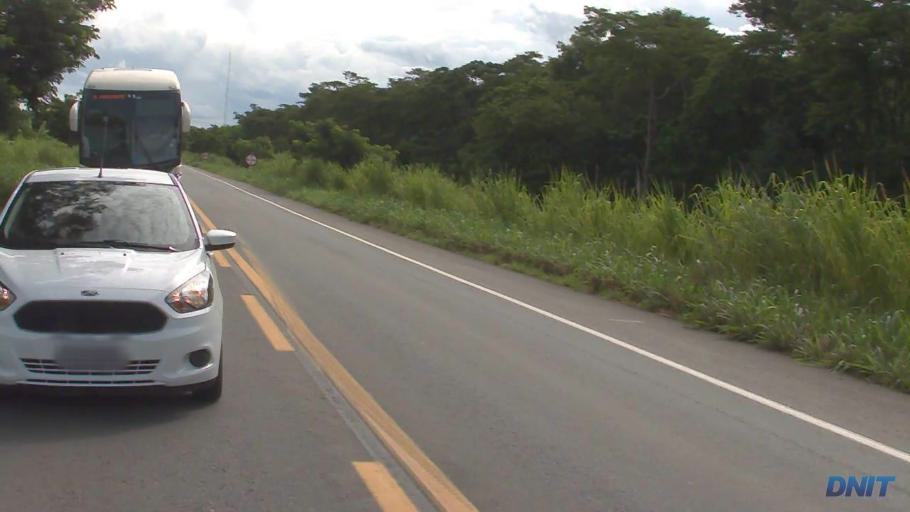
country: BR
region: Minas Gerais
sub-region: Ipaba
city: Ipaba
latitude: -19.3042
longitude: -42.3844
